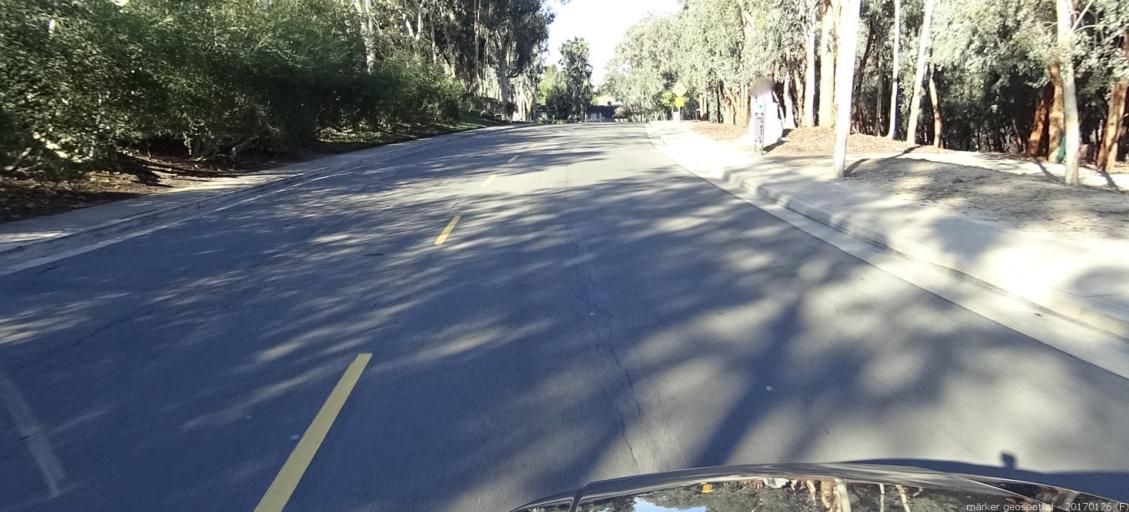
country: US
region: California
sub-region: Orange County
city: Lake Forest
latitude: 33.6475
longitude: -117.6990
